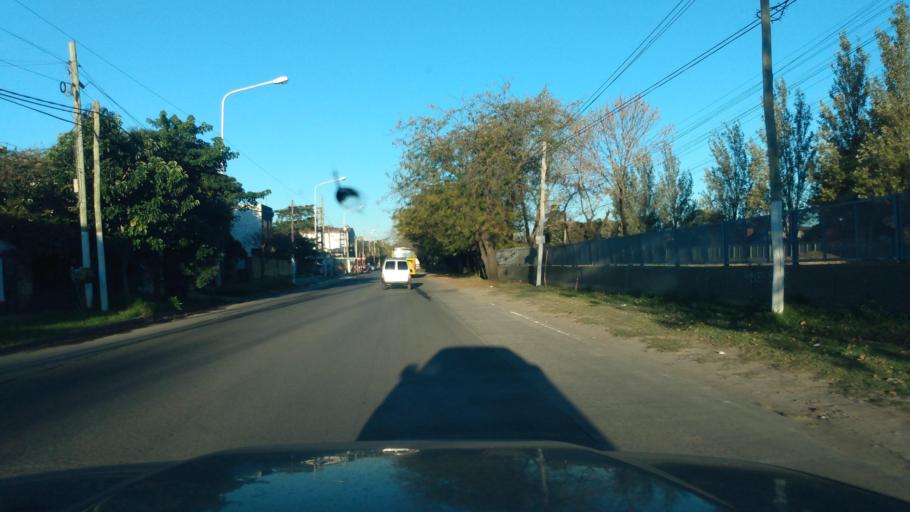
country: AR
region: Buenos Aires
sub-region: Partido de Merlo
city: Merlo
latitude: -34.6472
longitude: -58.8011
